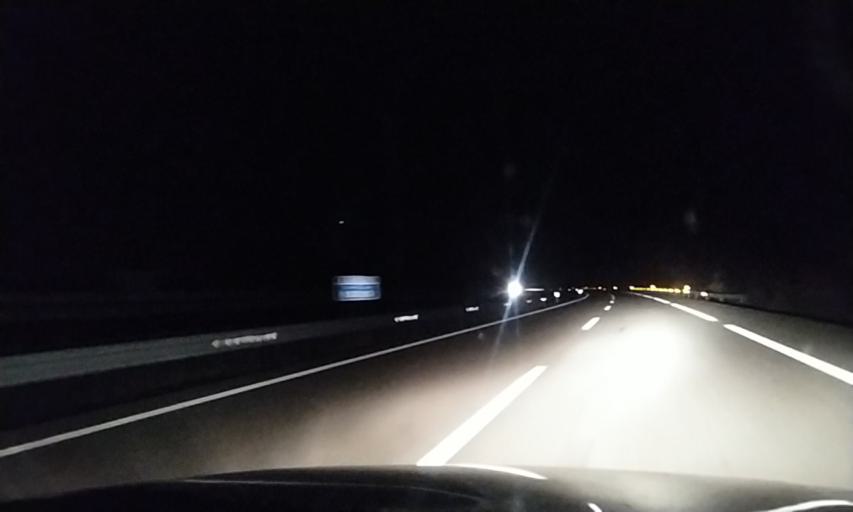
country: ES
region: Castille and Leon
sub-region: Provincia de Zamora
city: Puebla de Sanabria
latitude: 42.0625
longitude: -6.6475
